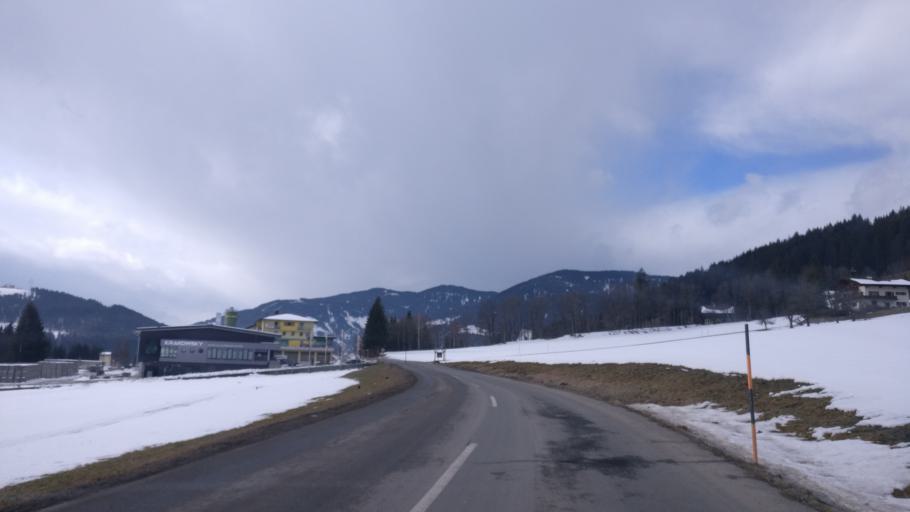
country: AT
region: Salzburg
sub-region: Politischer Bezirk Sankt Johann im Pongau
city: Radstadt
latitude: 47.3847
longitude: 13.4372
